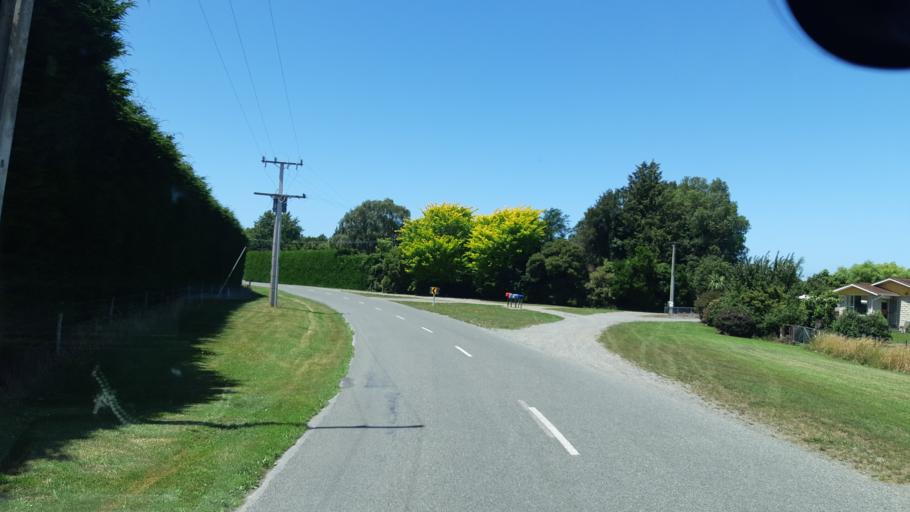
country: NZ
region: Canterbury
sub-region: Waimakariri District
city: Woodend
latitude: -43.2890
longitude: 172.6240
